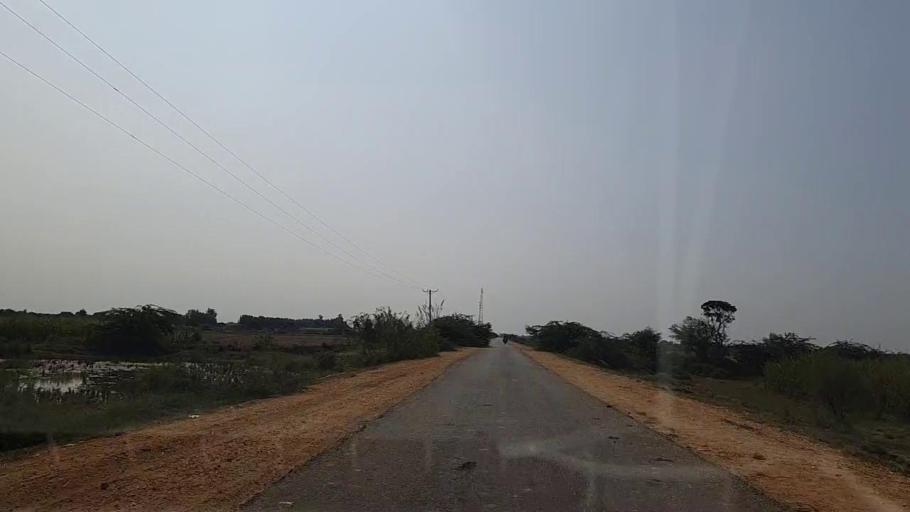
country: PK
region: Sindh
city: Chuhar Jamali
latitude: 24.2901
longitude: 67.9260
